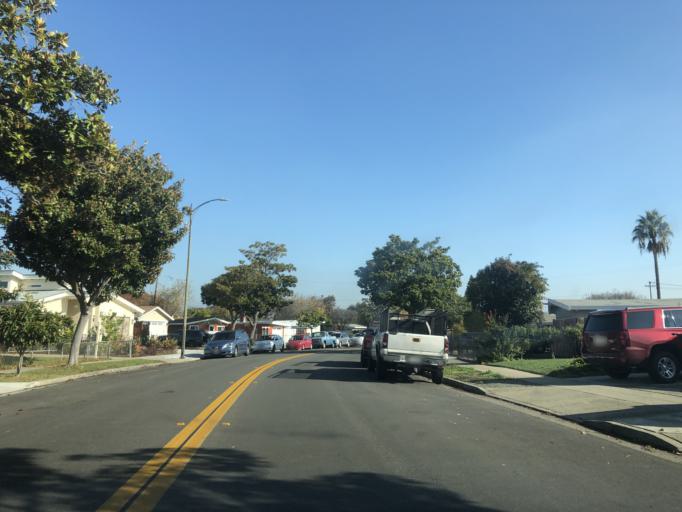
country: US
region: California
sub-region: Santa Clara County
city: Sunnyvale
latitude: 37.3935
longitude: -121.9976
